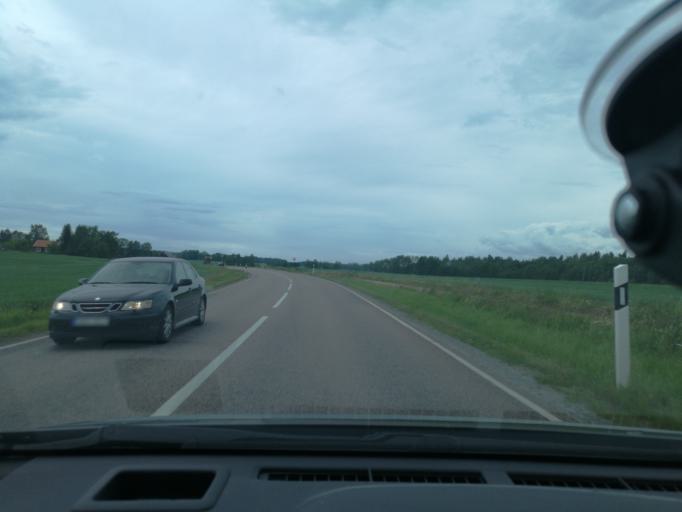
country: SE
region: Vaestmanland
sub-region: Vasteras
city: Skultuna
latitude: 59.6834
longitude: 16.4610
